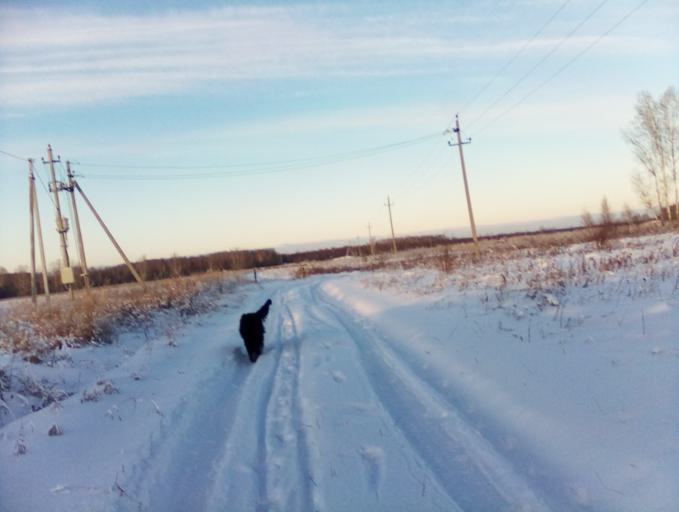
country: RU
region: Chelyabinsk
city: Poletayevo
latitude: 54.9848
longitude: 60.9468
